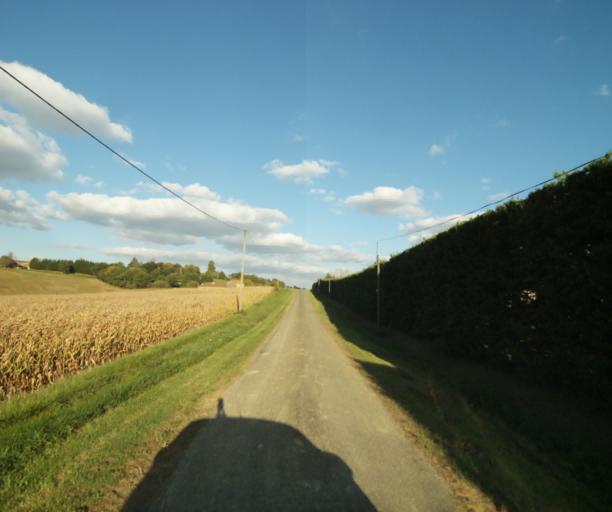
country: FR
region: Midi-Pyrenees
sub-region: Departement du Gers
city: Eauze
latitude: 43.7453
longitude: 0.1159
